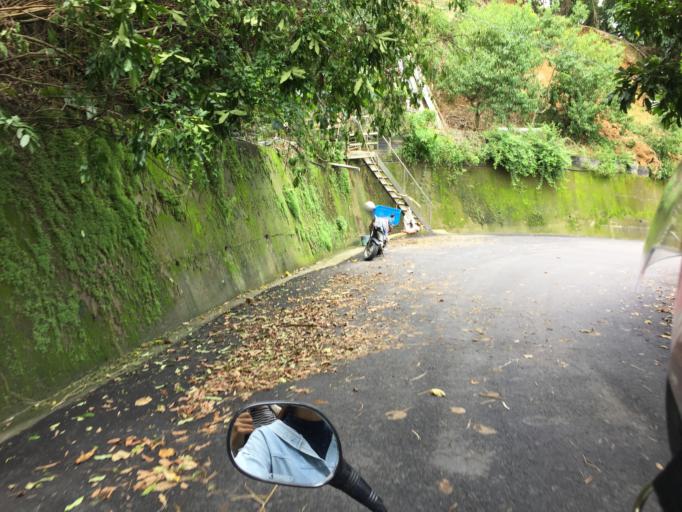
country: TW
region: Taiwan
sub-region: Taichung City
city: Taichung
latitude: 24.0659
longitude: 120.7059
